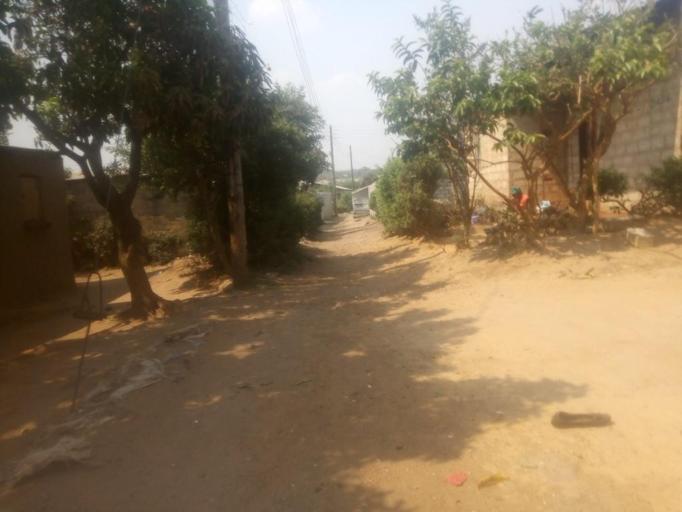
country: ZM
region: Lusaka
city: Lusaka
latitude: -15.4050
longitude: 28.3795
